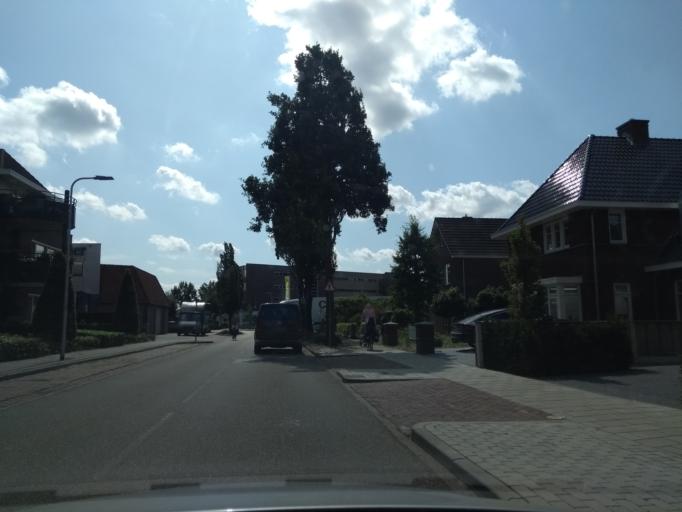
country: DE
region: Lower Saxony
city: Nordhorn
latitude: 52.3735
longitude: 7.0013
